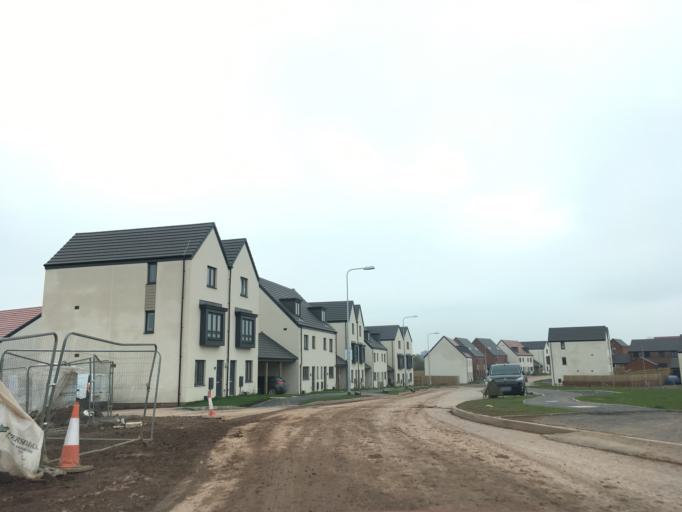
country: GB
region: Wales
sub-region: Newport
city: Marshfield
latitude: 51.5329
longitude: -3.1233
